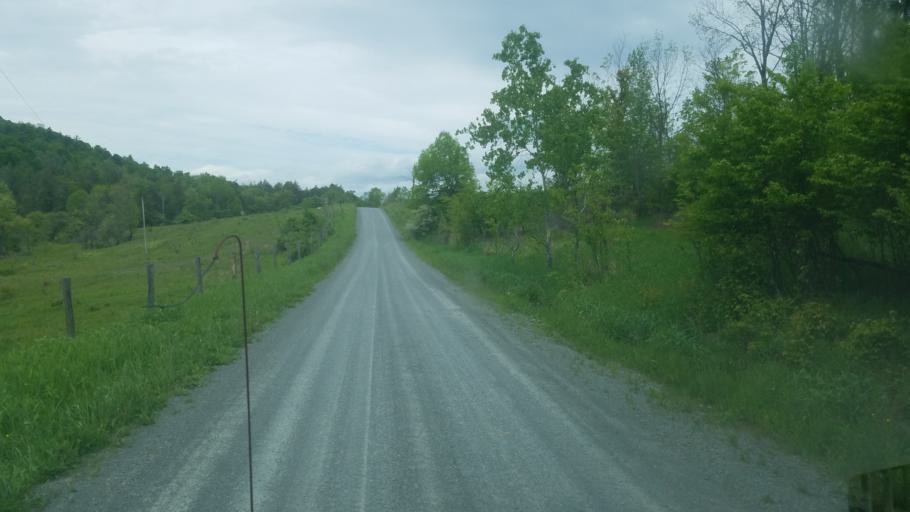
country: US
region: Pennsylvania
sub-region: Tioga County
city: Westfield
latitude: 41.8446
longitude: -77.6027
